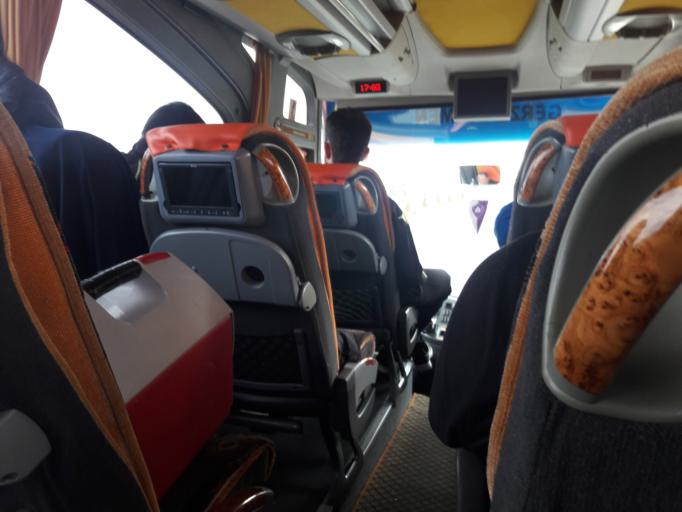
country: TR
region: Kastamonu
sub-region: Cide
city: Kastamonu
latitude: 41.3361
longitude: 33.7776
